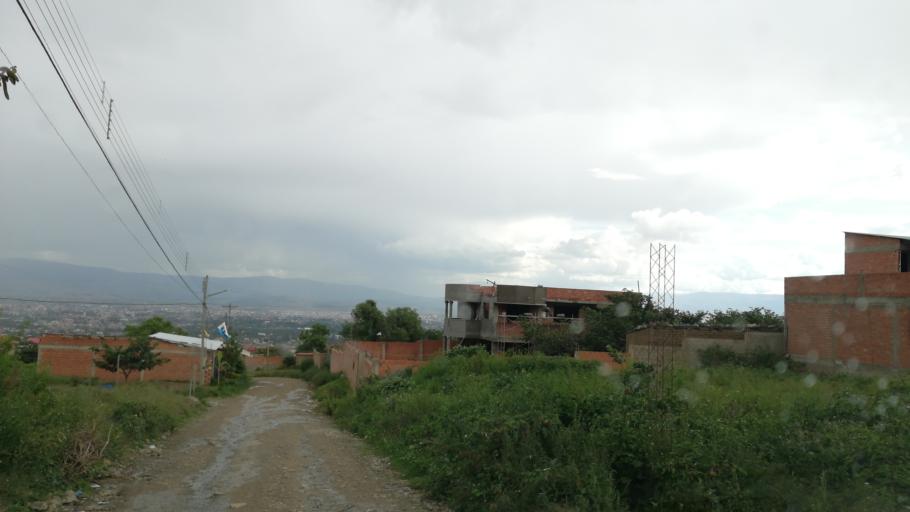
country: BO
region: Cochabamba
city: Cochabamba
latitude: -17.3280
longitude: -66.1926
